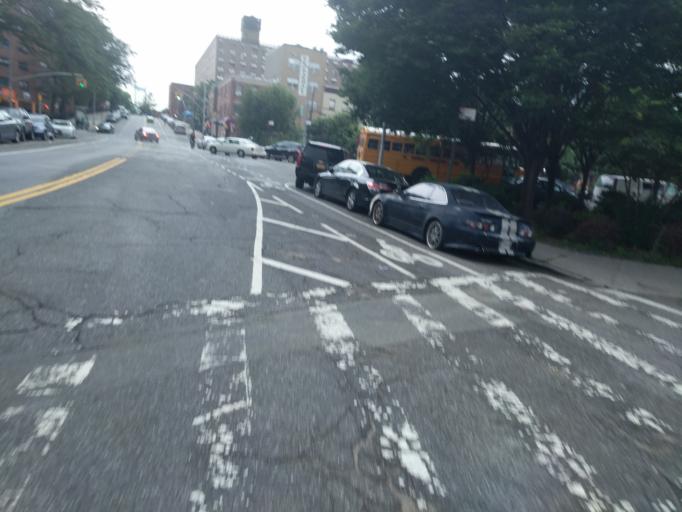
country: US
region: New York
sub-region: Queens County
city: Long Island City
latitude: 40.7721
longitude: -73.9330
